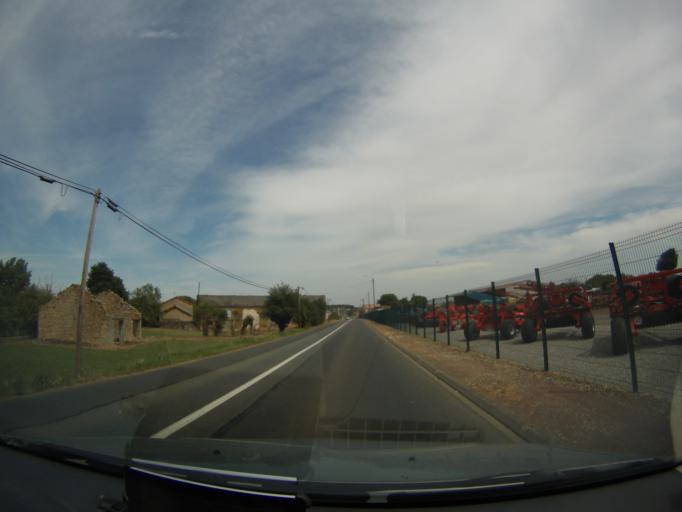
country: FR
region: Poitou-Charentes
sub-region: Departement de la Vienne
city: Moncontour
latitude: 46.8072
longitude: 0.0139
